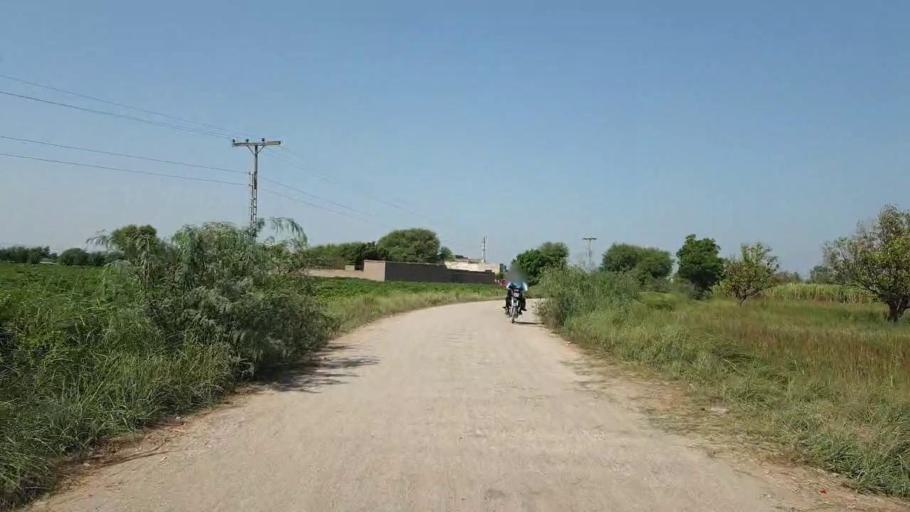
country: PK
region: Sindh
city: Tando Jam
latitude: 25.4944
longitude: 68.4637
